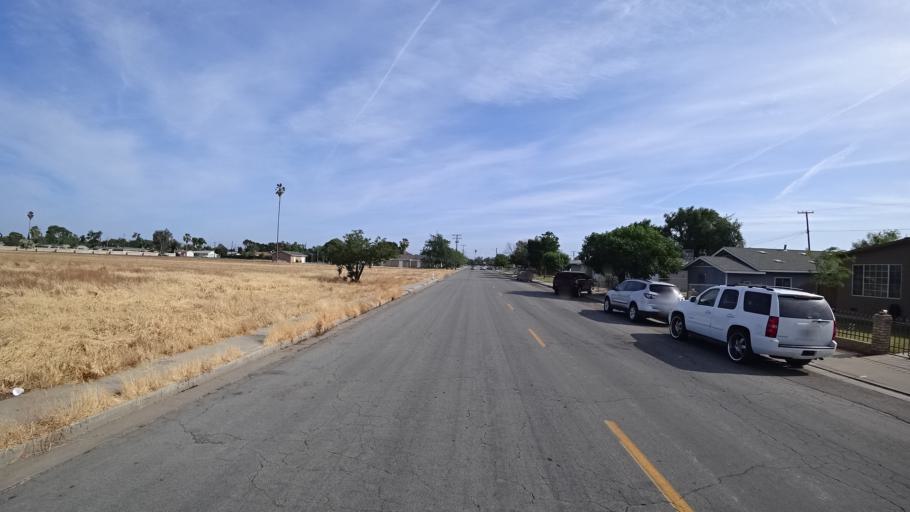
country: US
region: California
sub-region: Kings County
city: Hanford
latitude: 36.3167
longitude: -119.6426
